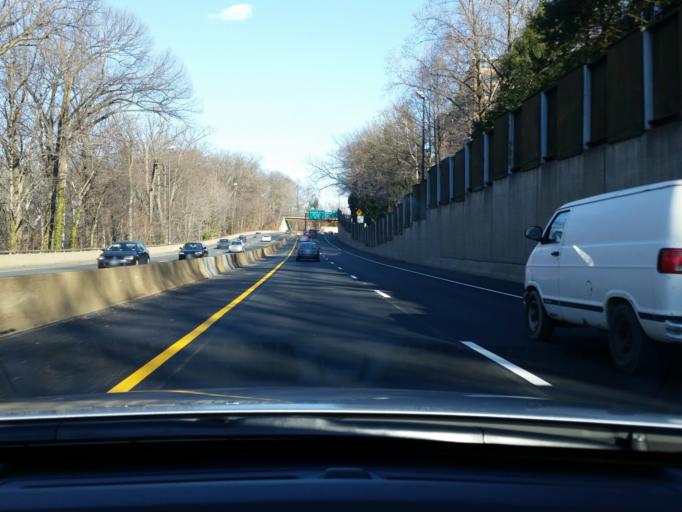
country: US
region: Virginia
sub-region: Arlington County
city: Arlington
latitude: 38.8981
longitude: -77.0915
